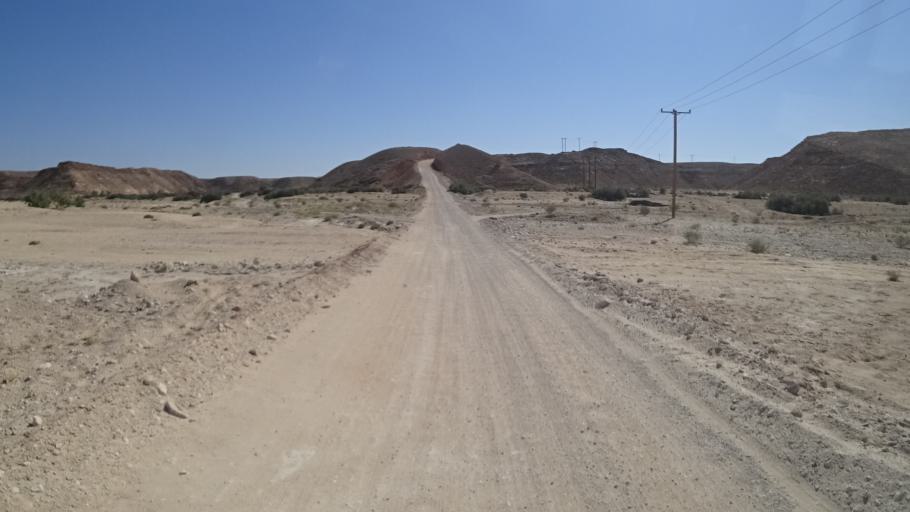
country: YE
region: Al Mahrah
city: Hawf
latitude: 17.3743
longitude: 53.1931
